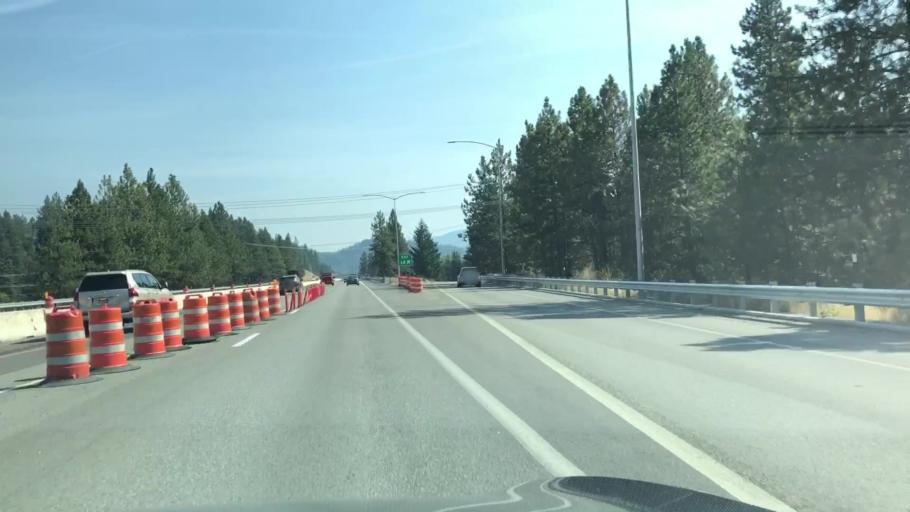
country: US
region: Idaho
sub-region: Kootenai County
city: Coeur d'Alene
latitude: 47.6909
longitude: -116.7672
